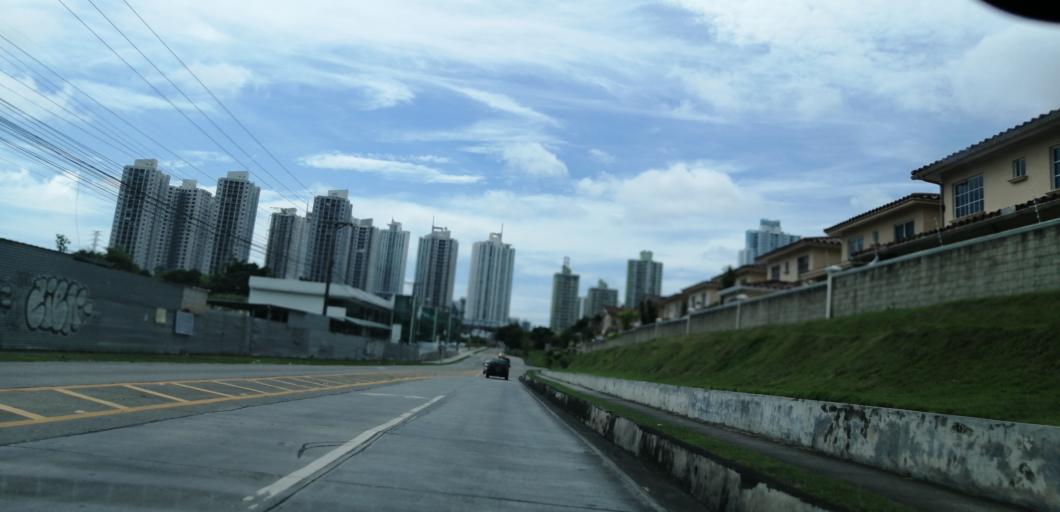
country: PA
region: Panama
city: Panama
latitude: 9.0336
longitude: -79.5275
